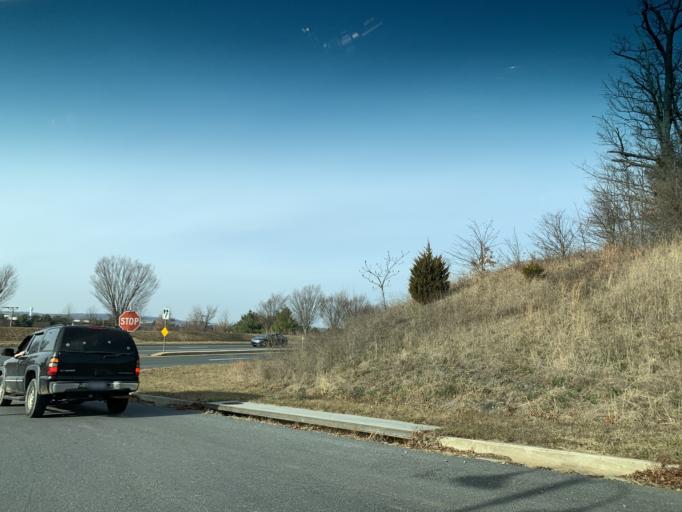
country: US
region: Maryland
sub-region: Carroll County
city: Westminster
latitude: 39.5713
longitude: -76.9736
